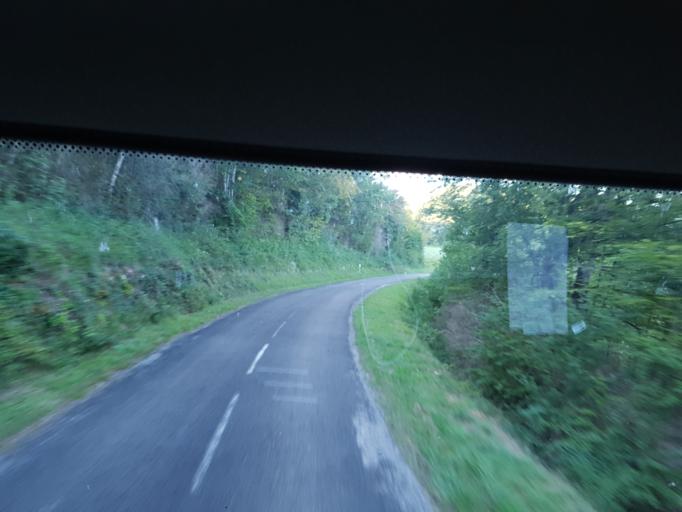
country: FR
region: Franche-Comte
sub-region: Departement du Jura
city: Orgelet
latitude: 46.4739
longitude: 5.6598
